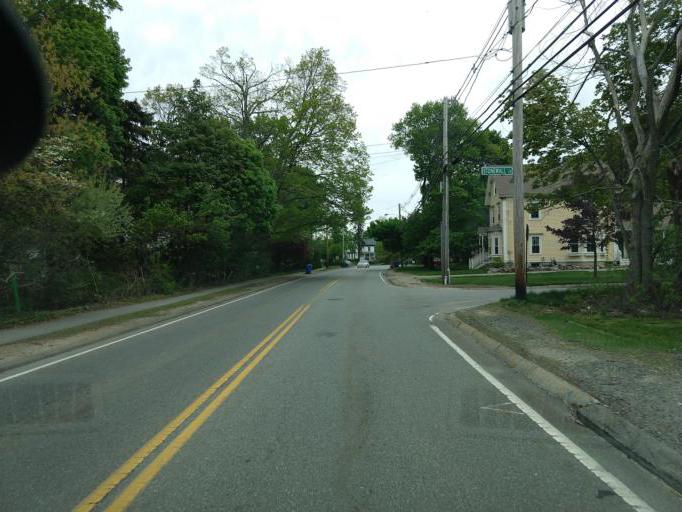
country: US
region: Massachusetts
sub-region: Middlesex County
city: Billerica
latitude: 42.5621
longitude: -71.2652
